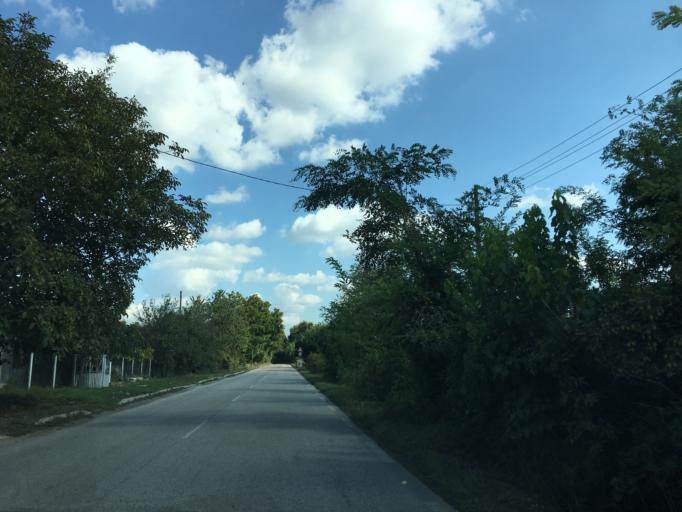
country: BG
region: Montana
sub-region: Obshtina Lom
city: Lom
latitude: 43.8223
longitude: 23.2021
